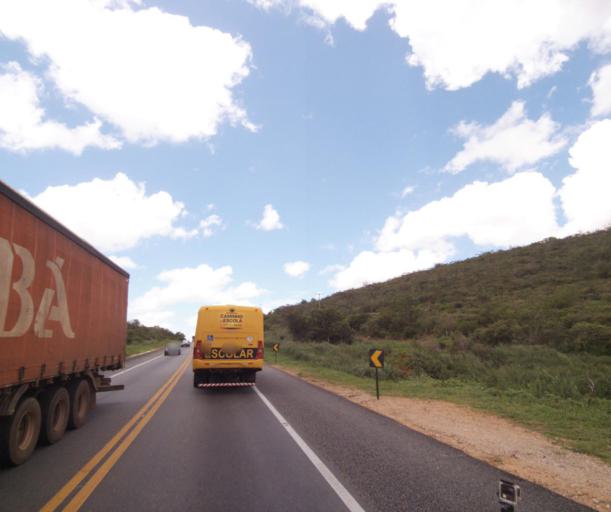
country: BR
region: Bahia
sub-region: Pocoes
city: Pocoes
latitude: -14.3634
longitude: -40.3425
